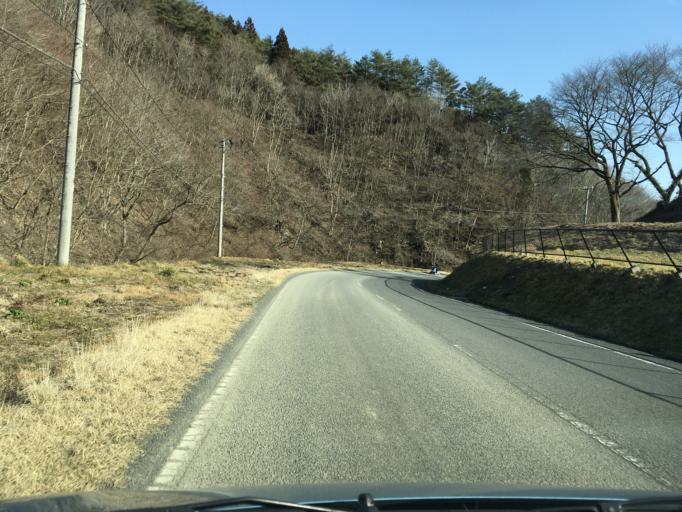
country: JP
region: Iwate
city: Ichinoseki
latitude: 38.7914
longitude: 141.4504
